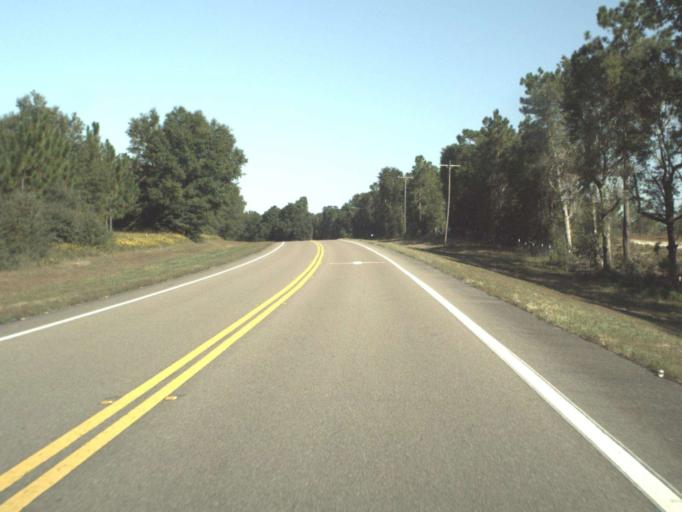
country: US
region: Florida
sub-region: Walton County
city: Freeport
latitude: 30.5498
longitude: -85.9154
